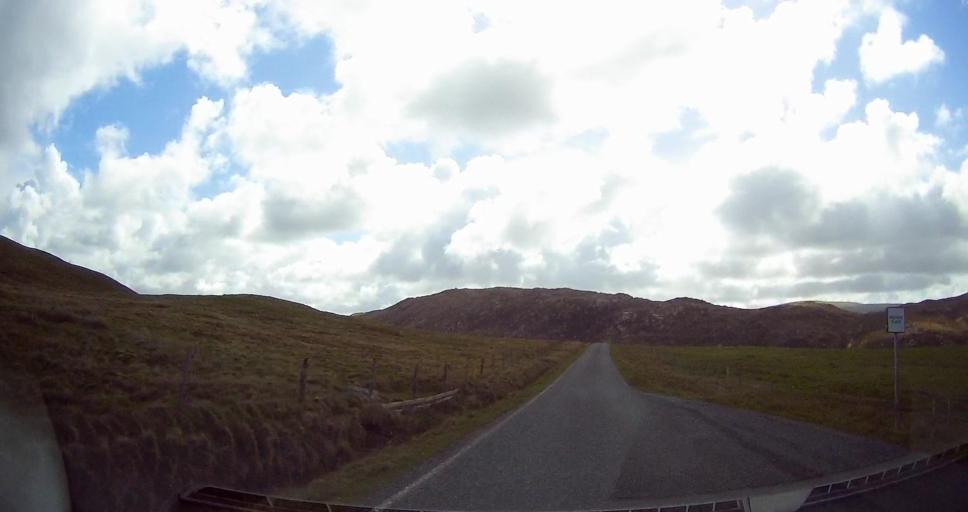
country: GB
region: Scotland
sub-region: Shetland Islands
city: Lerwick
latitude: 60.5583
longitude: -1.3359
